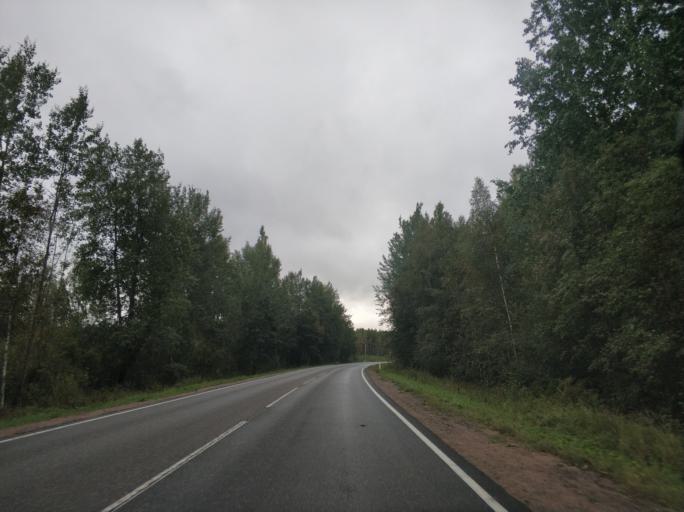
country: RU
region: Leningrad
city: Borisova Griva
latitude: 60.1161
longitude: 30.9637
